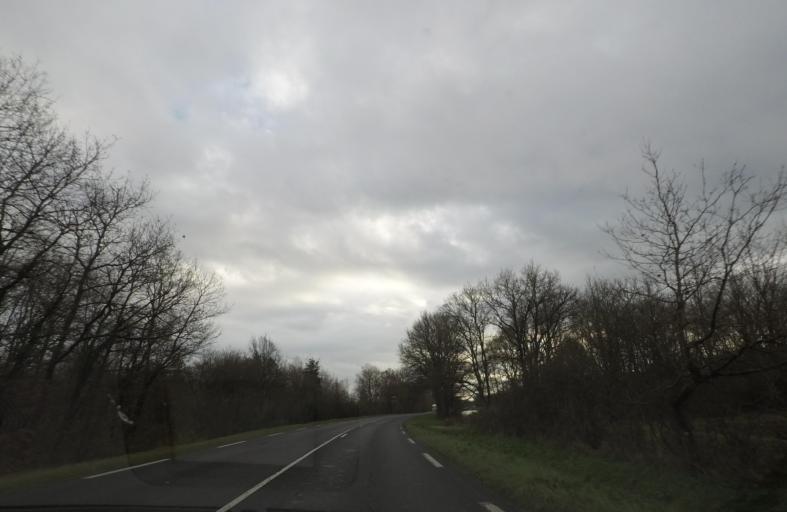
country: FR
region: Centre
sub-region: Departement du Loir-et-Cher
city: Soings-en-Sologne
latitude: 47.4378
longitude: 1.5545
